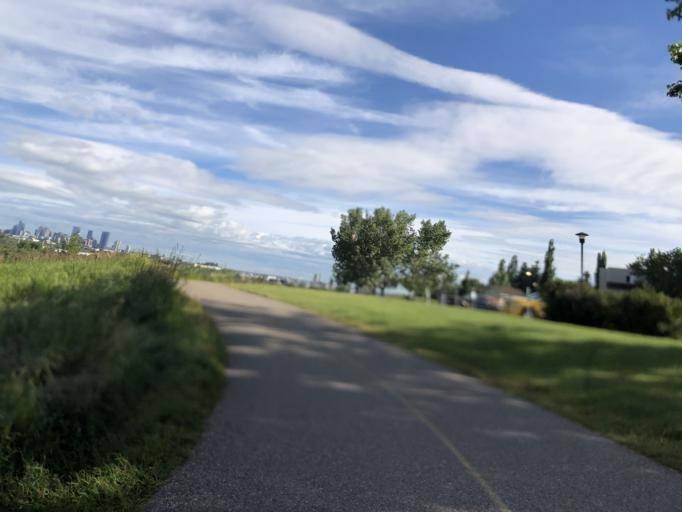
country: CA
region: Alberta
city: Calgary
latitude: 50.9963
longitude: -114.0230
